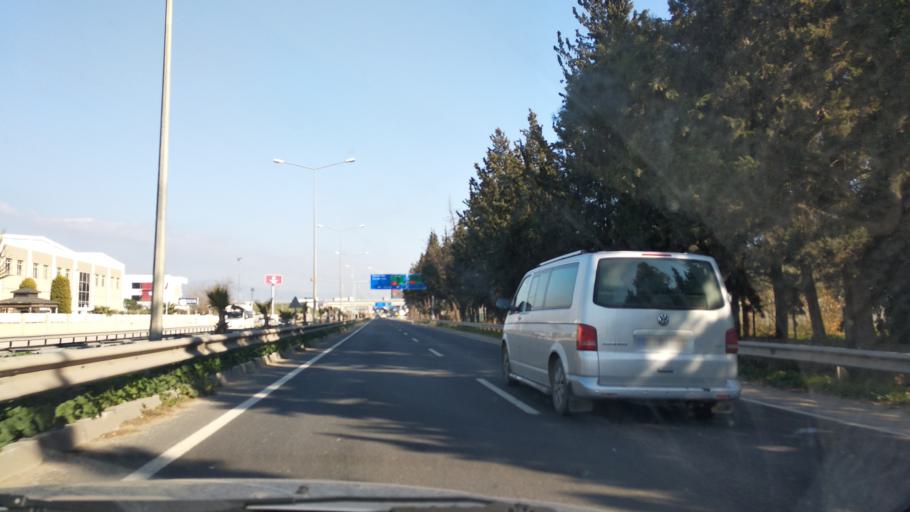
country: TR
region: Izmir
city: Menemen
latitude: 38.5677
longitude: 27.0532
